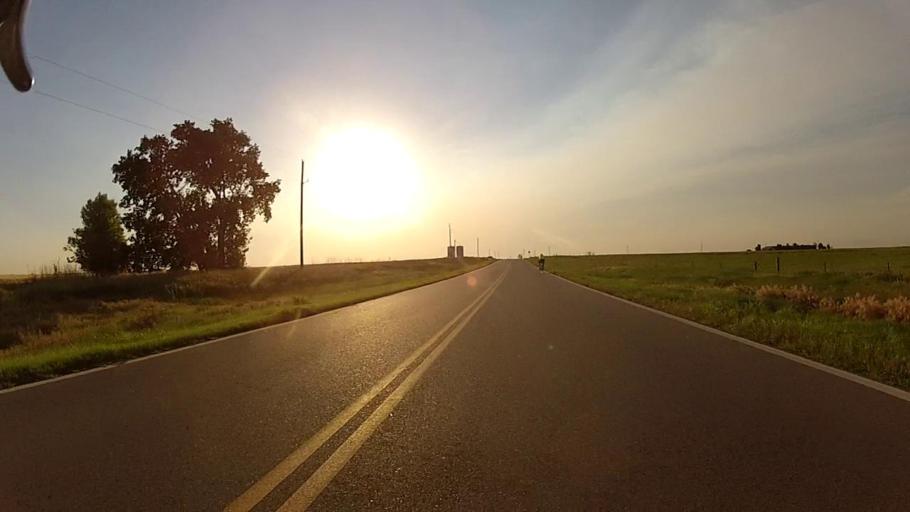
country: US
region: Kansas
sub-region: Harper County
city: Anthony
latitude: 37.1534
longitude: -97.8795
